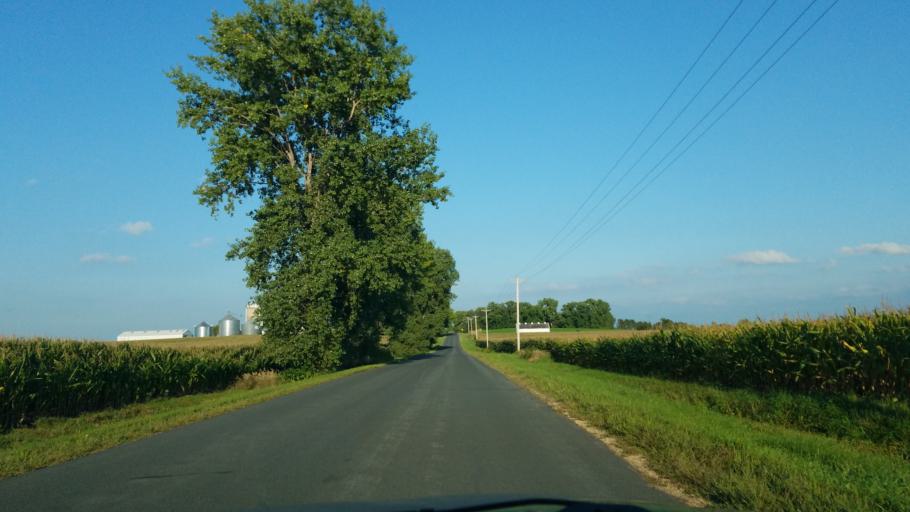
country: US
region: Wisconsin
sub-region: Saint Croix County
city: Roberts
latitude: 45.0071
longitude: -92.5472
